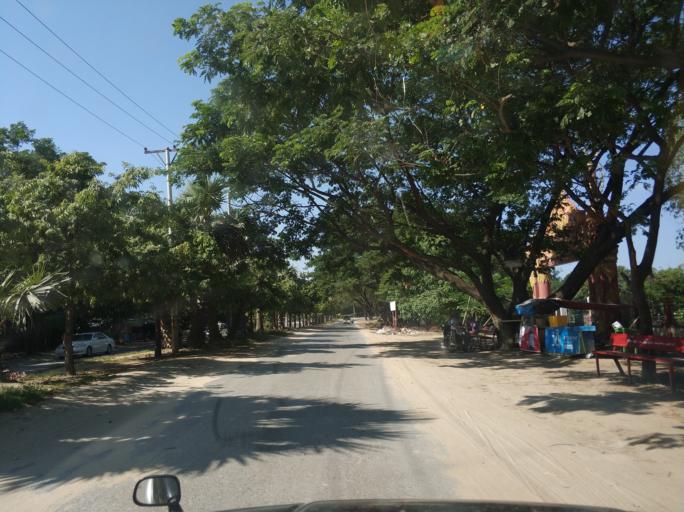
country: MM
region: Mandalay
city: Mandalay
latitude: 21.9574
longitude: 96.0524
